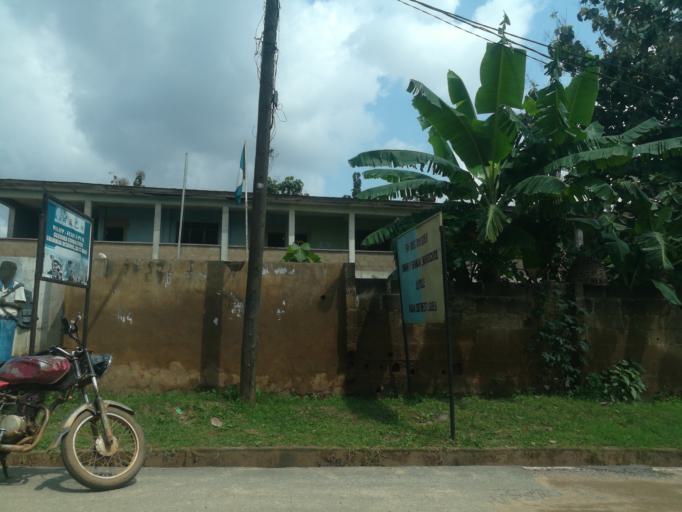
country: NG
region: Oyo
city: Ibadan
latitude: 7.3633
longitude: 3.8559
